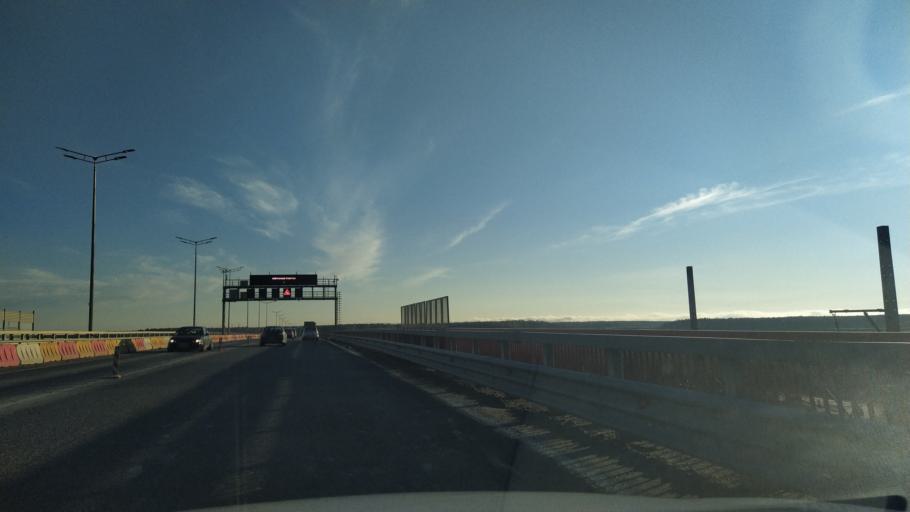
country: RU
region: St.-Petersburg
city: Pargolovo
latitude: 60.0922
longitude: 30.2454
